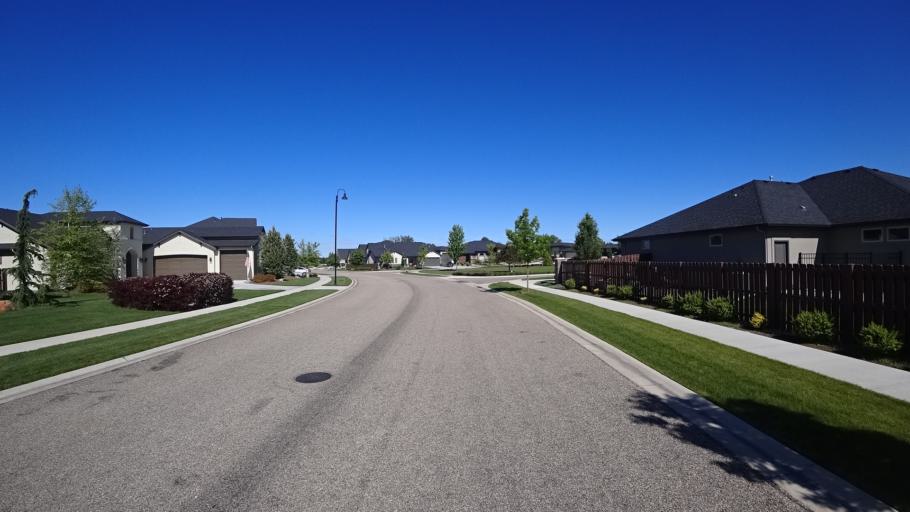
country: US
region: Idaho
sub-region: Ada County
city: Meridian
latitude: 43.6677
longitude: -116.4068
